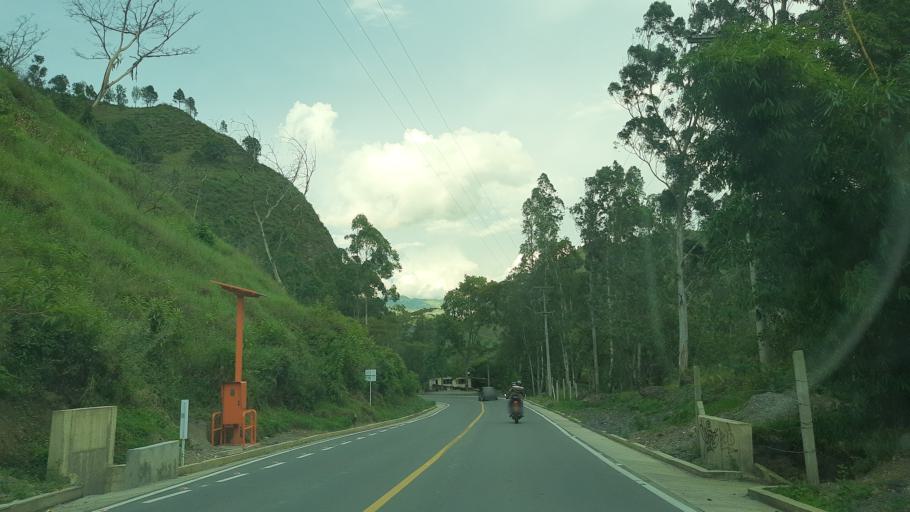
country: CO
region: Boyaca
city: Somondoco
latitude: 5.0093
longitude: -73.3994
